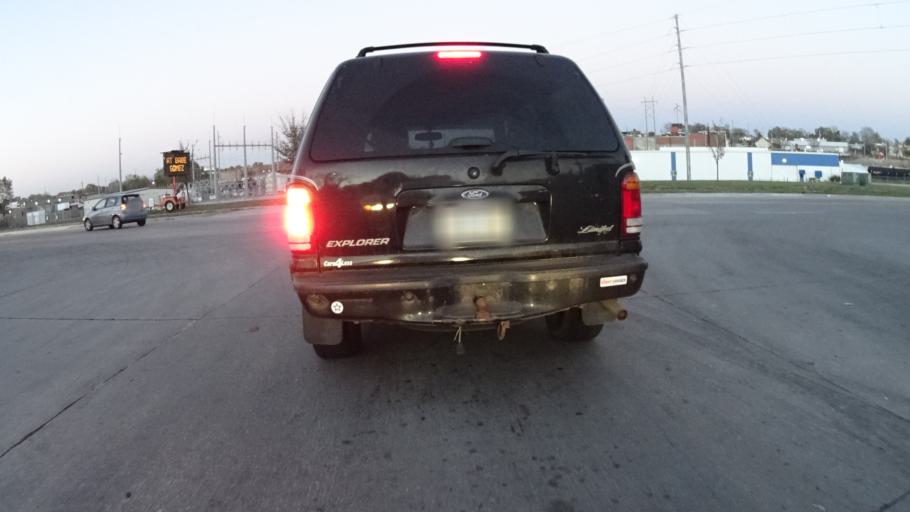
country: US
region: Nebraska
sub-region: Douglas County
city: Omaha
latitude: 41.2063
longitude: -95.9529
